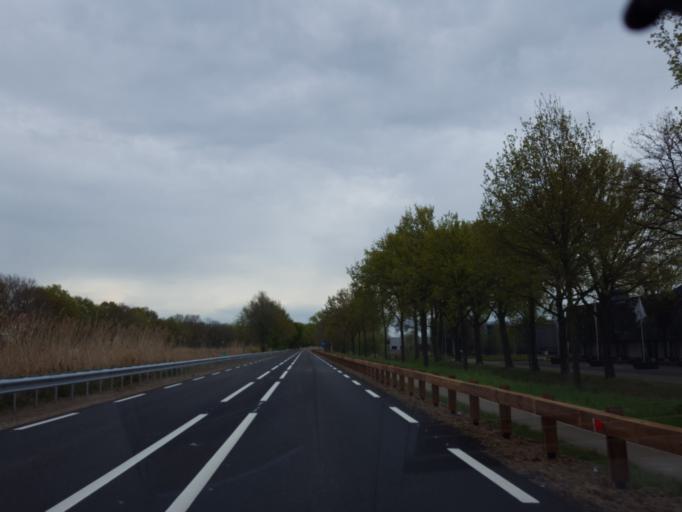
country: NL
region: North Brabant
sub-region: Gemeente Someren
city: Someren
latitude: 51.3941
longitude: 5.7291
